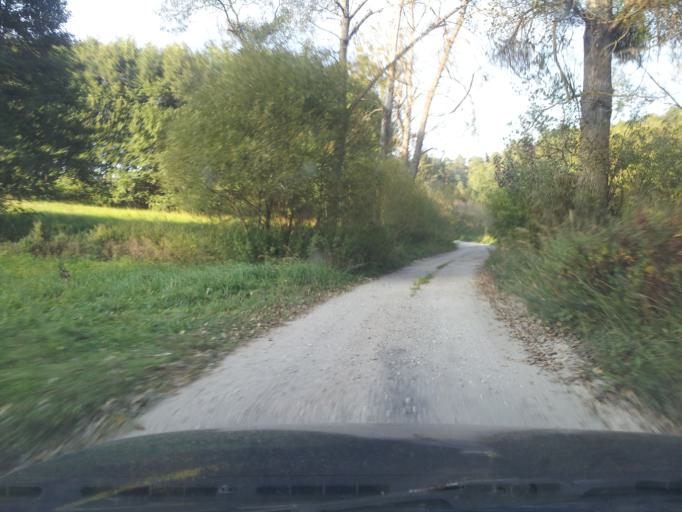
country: PL
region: Kujawsko-Pomorskie
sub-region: Powiat brodnicki
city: Gorzno
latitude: 53.2033
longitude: 19.6423
